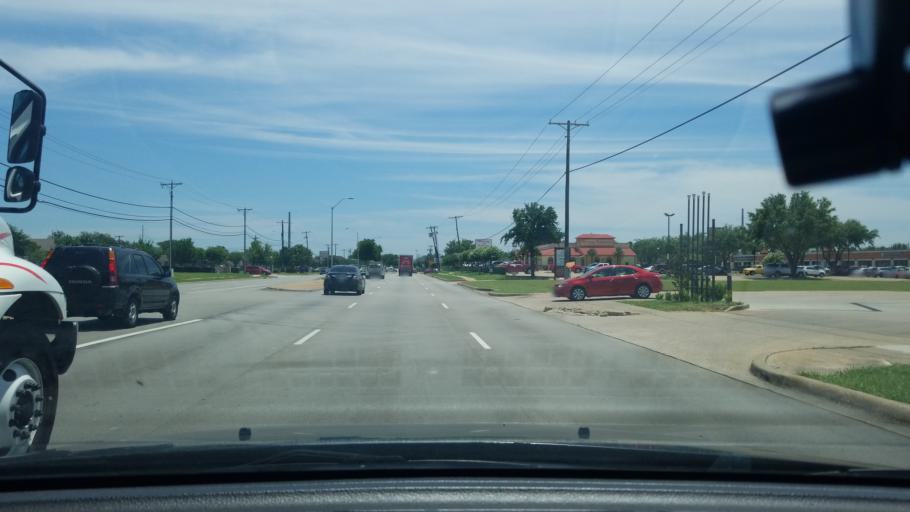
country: US
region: Texas
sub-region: Dallas County
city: Mesquite
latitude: 32.7782
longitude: -96.6210
